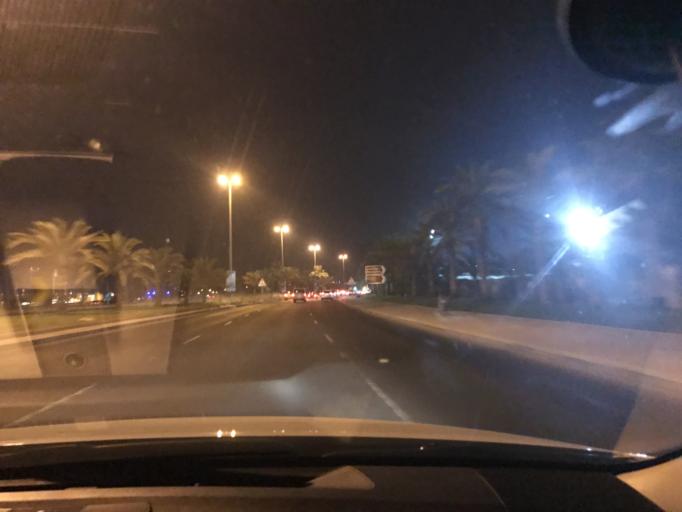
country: BH
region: Muharraq
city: Al Muharraq
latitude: 26.2431
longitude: 50.6125
